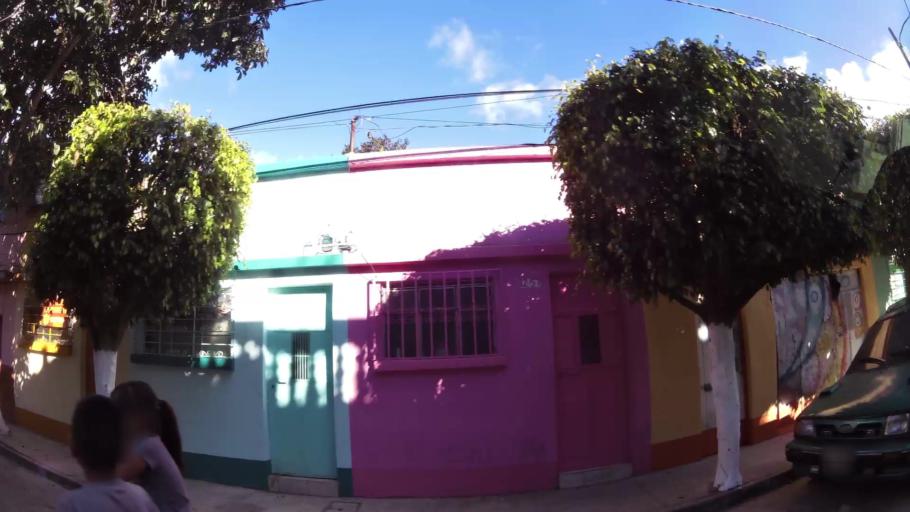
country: GT
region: Guatemala
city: Guatemala City
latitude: 14.6346
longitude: -90.5023
